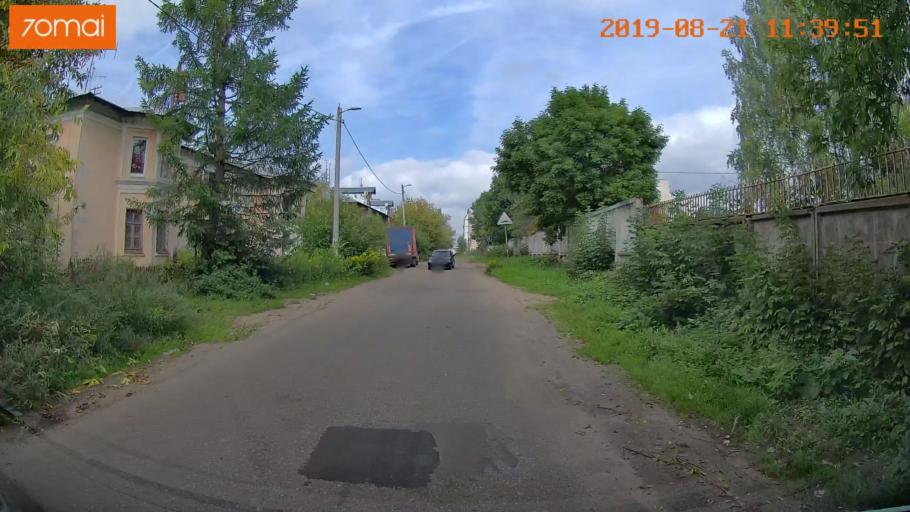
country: RU
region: Ivanovo
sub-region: Gorod Ivanovo
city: Ivanovo
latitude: 57.0006
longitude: 40.9377
